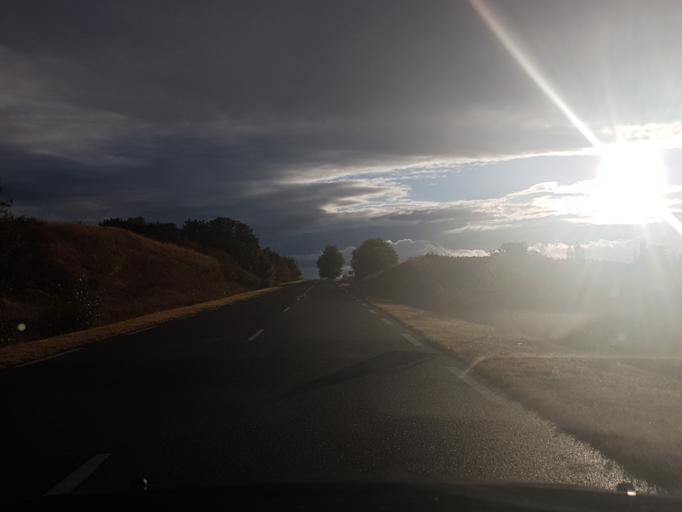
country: FR
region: Languedoc-Roussillon
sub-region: Departement de l'Aude
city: Bram
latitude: 43.1743
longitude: 2.0102
